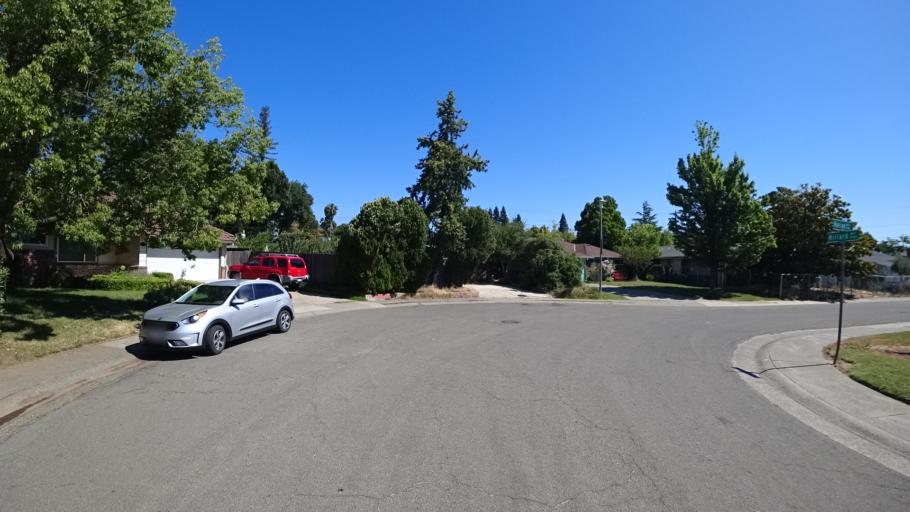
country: US
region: California
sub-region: Sacramento County
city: Parkway
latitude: 38.5287
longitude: -121.4993
